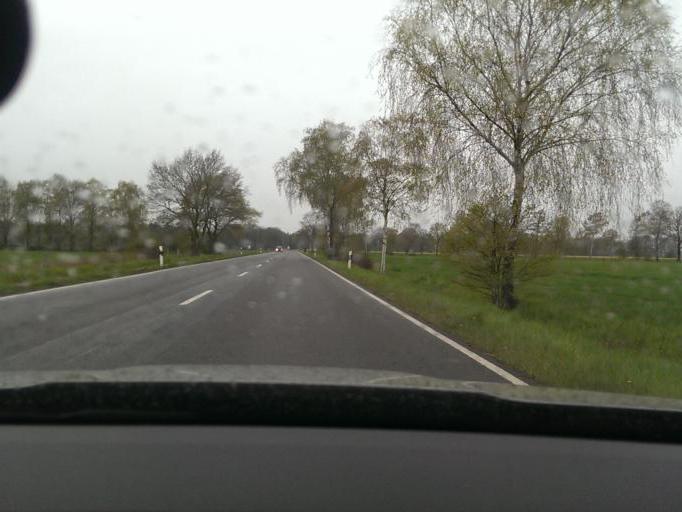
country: DE
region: Lower Saxony
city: Gilten
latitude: 52.6690
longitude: 9.5110
